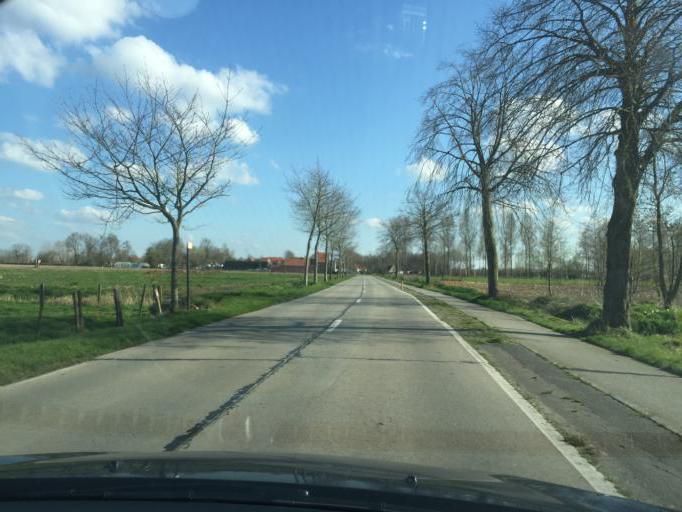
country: BE
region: Flanders
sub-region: Provincie West-Vlaanderen
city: Beernem
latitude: 51.1616
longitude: 3.3166
